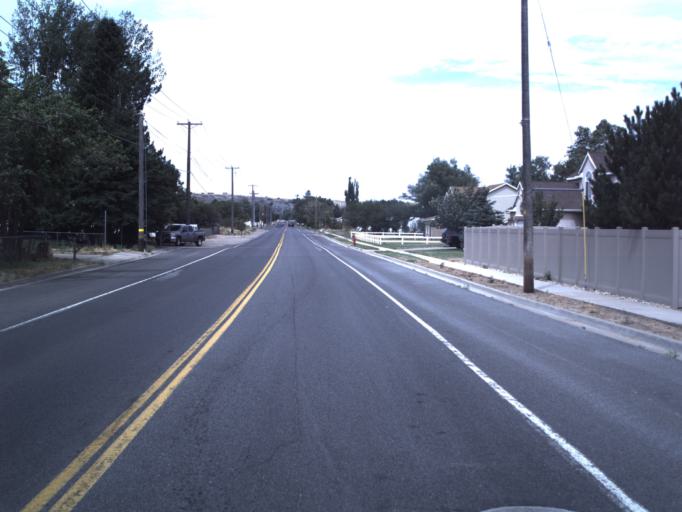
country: US
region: Utah
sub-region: Davis County
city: South Weber
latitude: 41.1325
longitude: -111.9264
